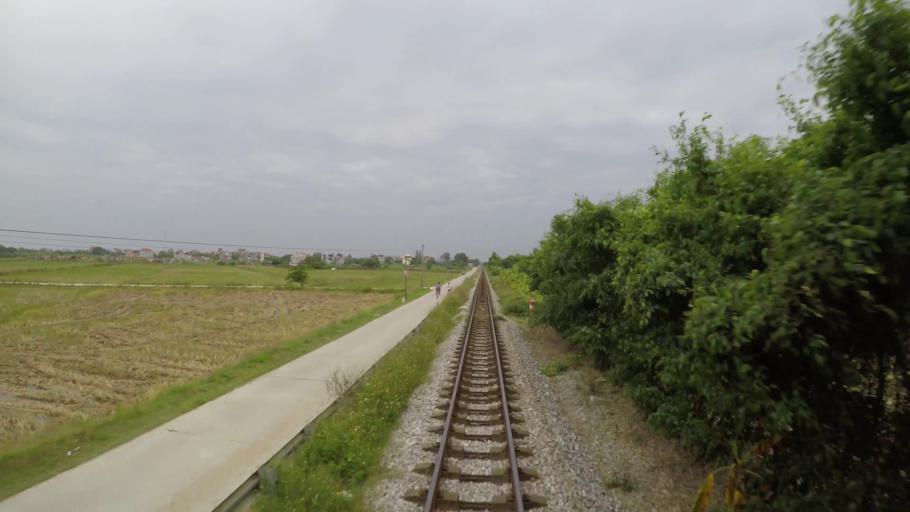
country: VN
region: Hai Duong
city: Lai Cach
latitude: 20.9523
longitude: 106.2315
